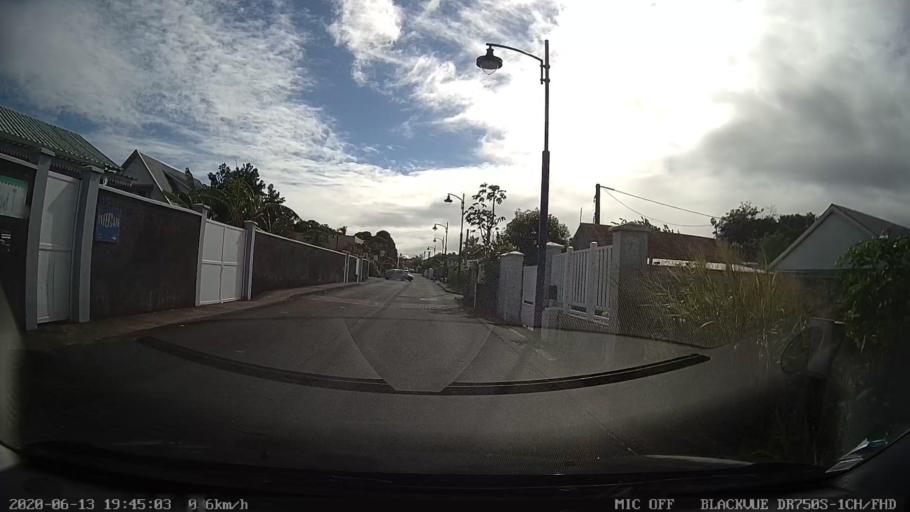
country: RE
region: Reunion
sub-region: Reunion
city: Bras-Panon
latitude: -20.9988
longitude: 55.6767
